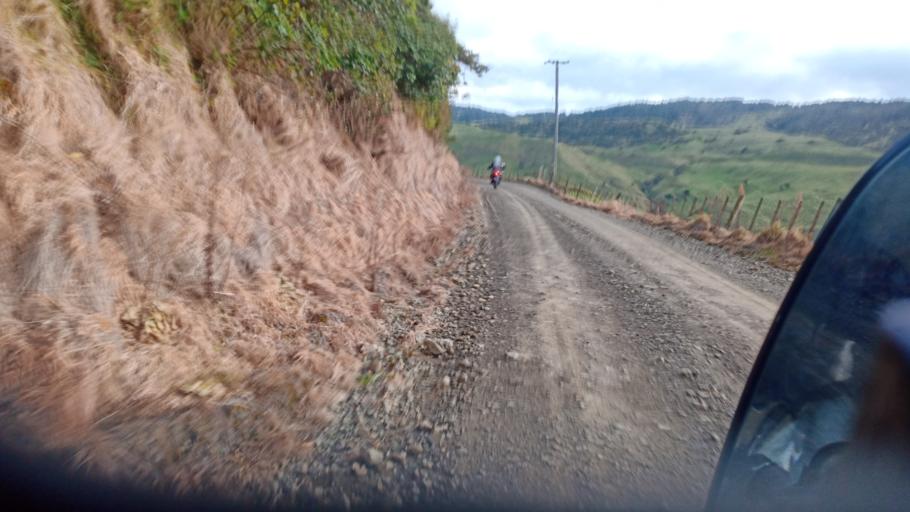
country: NZ
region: Gisborne
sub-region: Gisborne District
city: Gisborne
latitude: -38.4706
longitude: 177.5266
